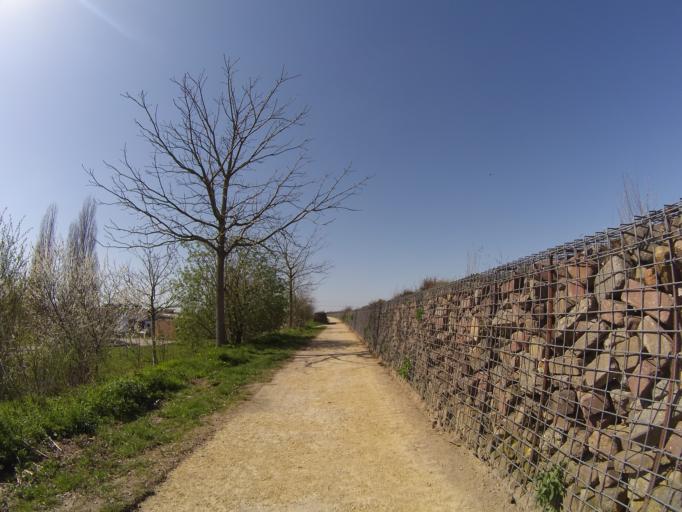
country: NL
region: Utrecht
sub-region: Gemeente Amersfoort
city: Hoogland
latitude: 52.2057
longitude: 5.3801
